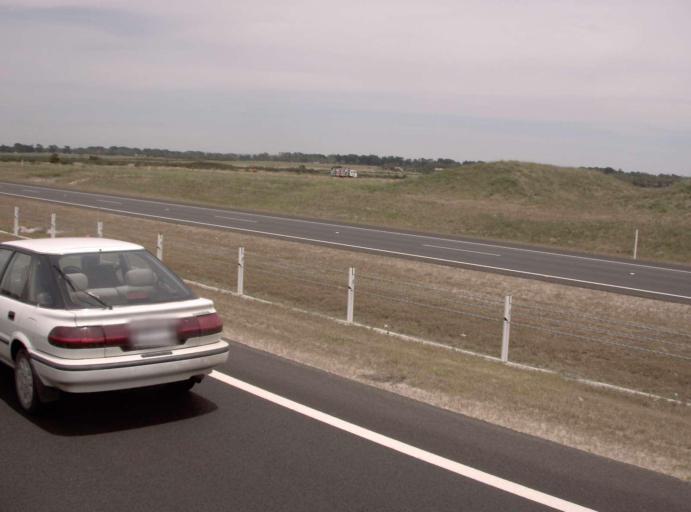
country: AU
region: Victoria
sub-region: Mornington Peninsula
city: Moorooduc
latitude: -38.2347
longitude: 145.1248
